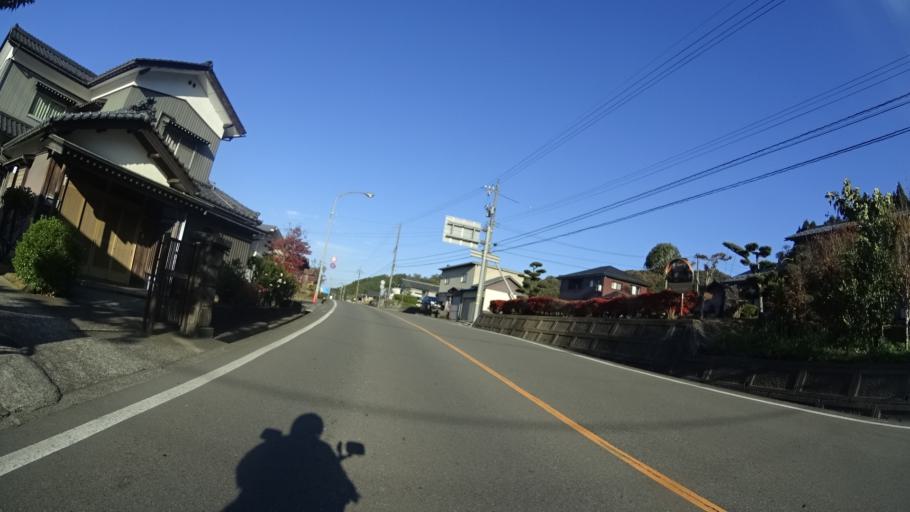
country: JP
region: Fukui
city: Maruoka
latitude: 36.1051
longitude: 136.3280
